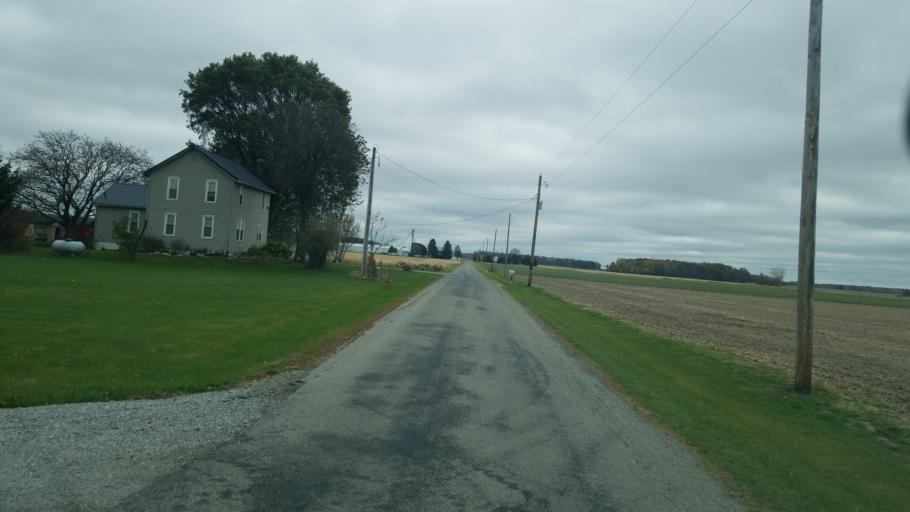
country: US
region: Ohio
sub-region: Huron County
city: Willard
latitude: 40.9314
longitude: -82.8331
